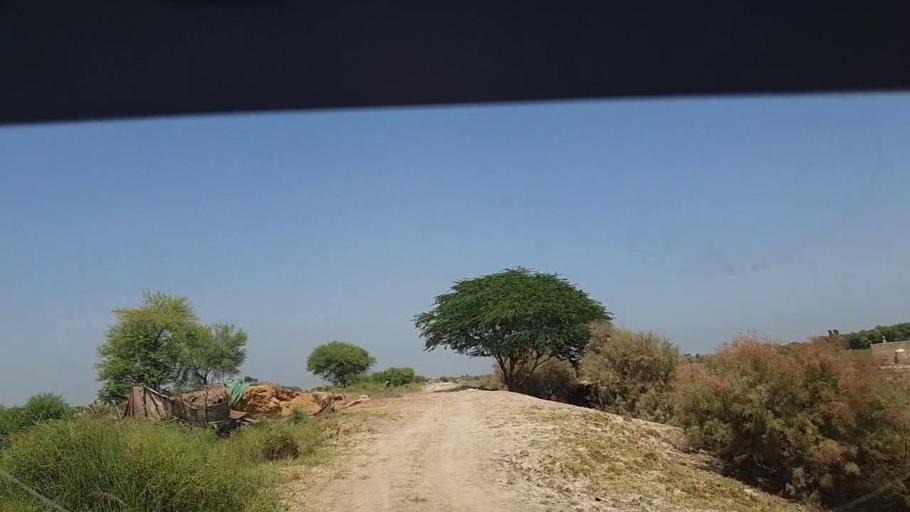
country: PK
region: Sindh
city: Kandhkot
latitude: 28.1806
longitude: 69.1532
